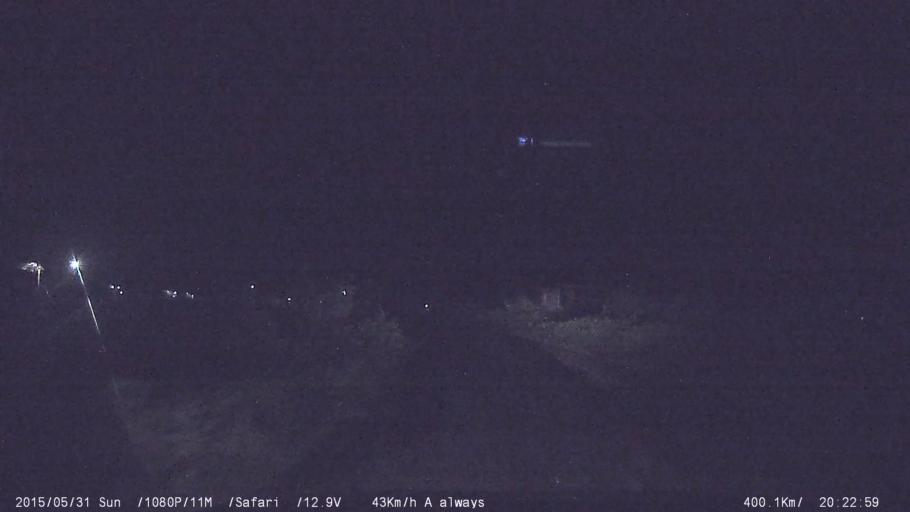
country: IN
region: Karnataka
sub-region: Mandya
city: Malavalli
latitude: 12.4254
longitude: 77.2225
